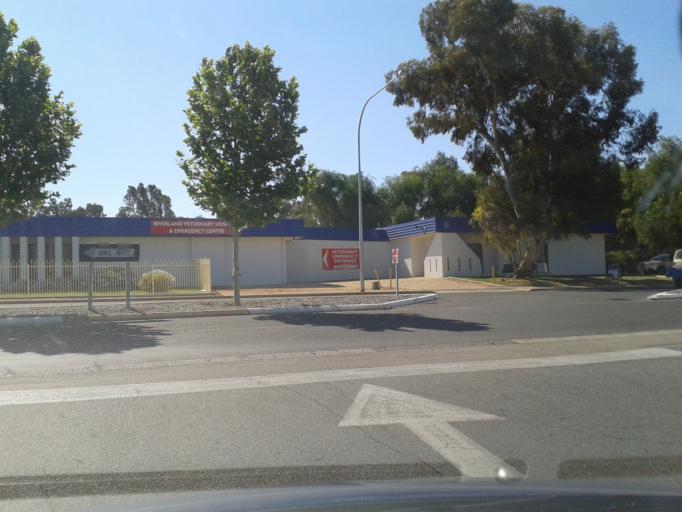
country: AU
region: South Australia
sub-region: Berri and Barmera
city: Berri
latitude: -34.2795
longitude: 140.6087
